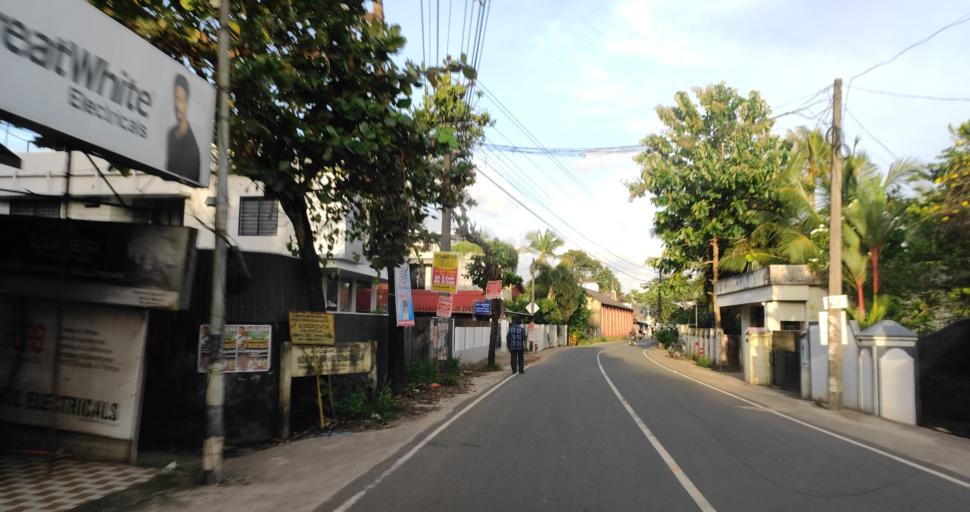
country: IN
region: Kerala
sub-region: Alappuzha
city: Shertallai
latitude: 9.6069
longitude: 76.3559
